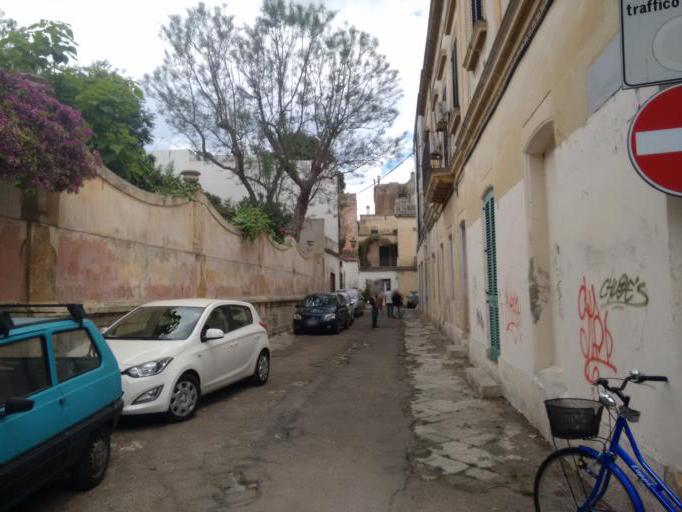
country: IT
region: Apulia
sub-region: Provincia di Lecce
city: Lecce
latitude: 40.3550
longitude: 18.1676
